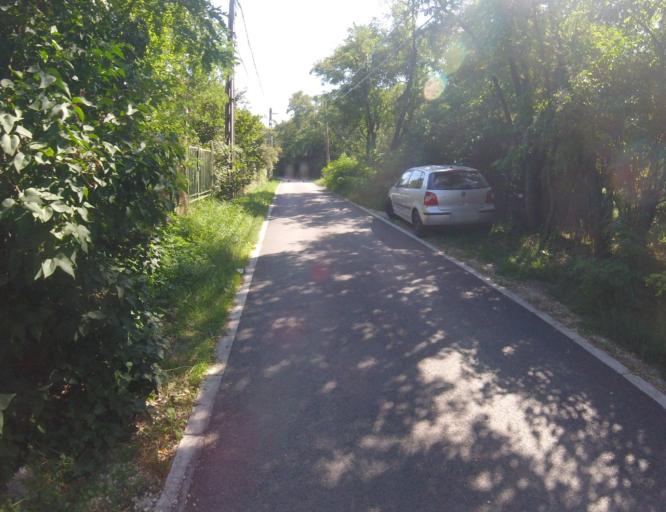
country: HU
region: Fejer
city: Velence
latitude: 47.2510
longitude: 18.6115
